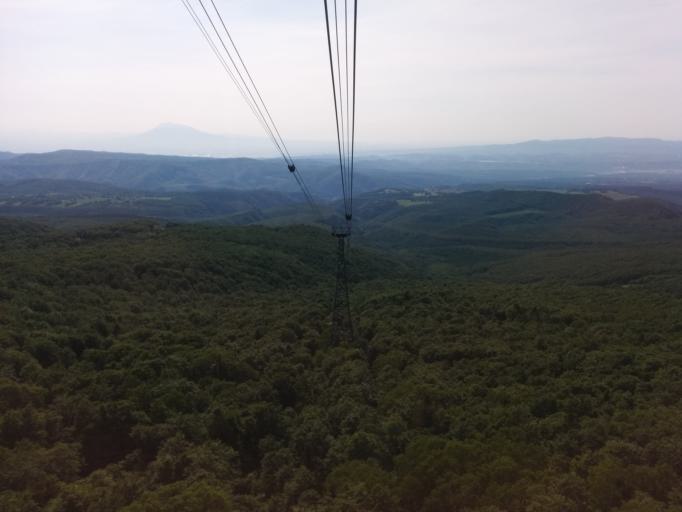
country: JP
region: Aomori
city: Aomori Shi
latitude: 40.6777
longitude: 140.8489
